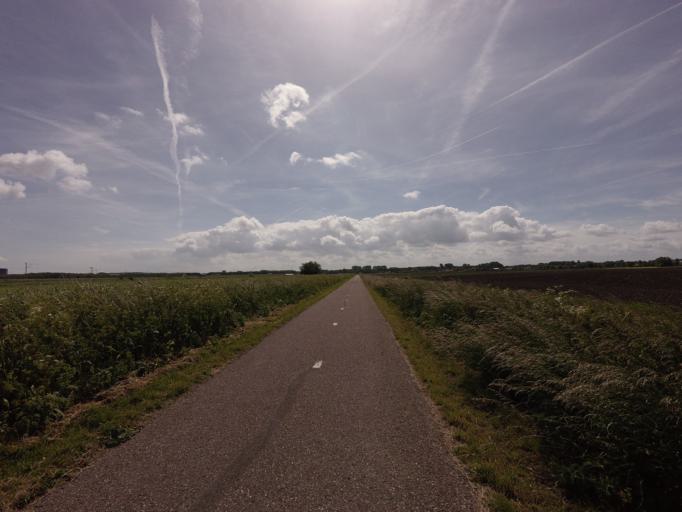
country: NL
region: North Holland
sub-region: Gemeente Hoorn
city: Hoorn
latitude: 52.6499
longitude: 5.0164
